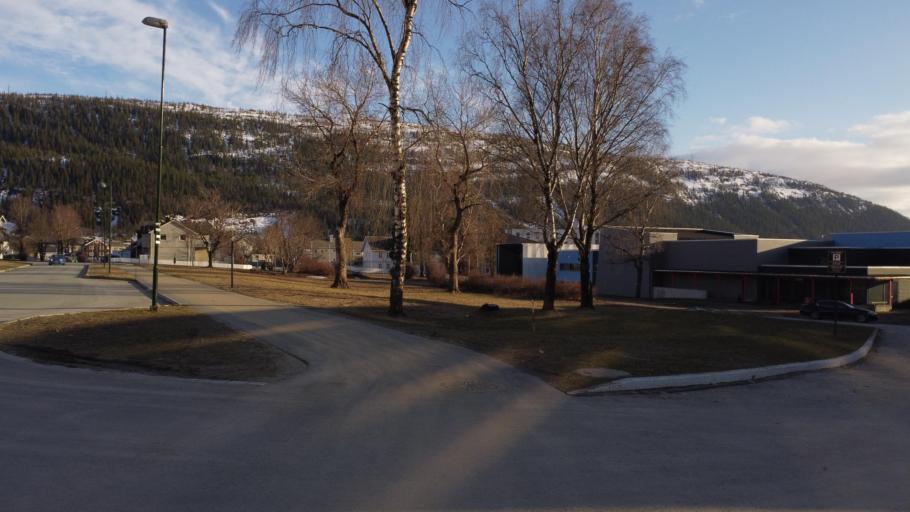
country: NO
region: Nordland
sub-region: Rana
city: Mo i Rana
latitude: 66.3110
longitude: 14.1417
